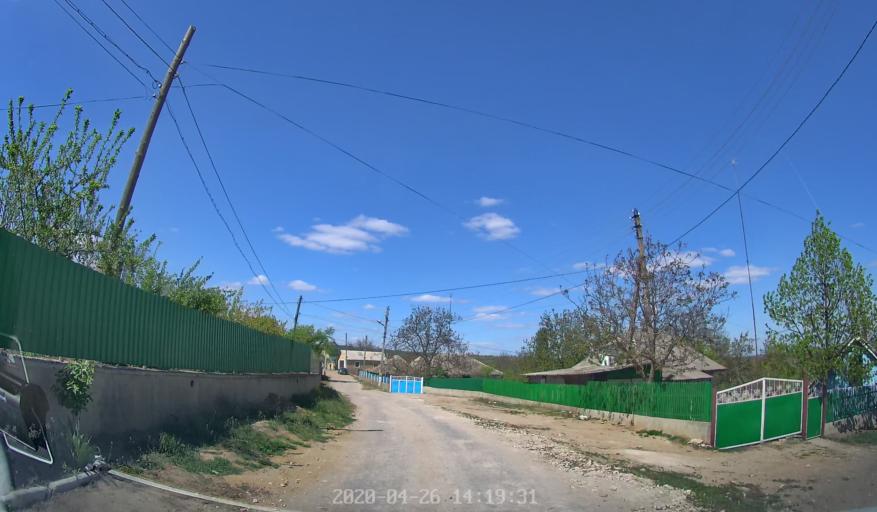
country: MD
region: Telenesti
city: Cocieri
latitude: 47.3559
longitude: 29.0597
